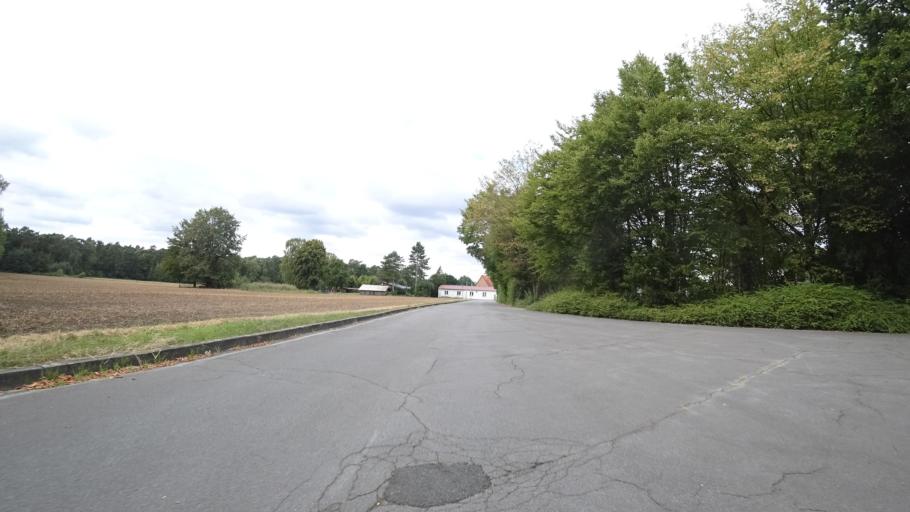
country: DE
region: North Rhine-Westphalia
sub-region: Regierungsbezirk Detmold
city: Verl
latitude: 51.9344
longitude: 8.4666
